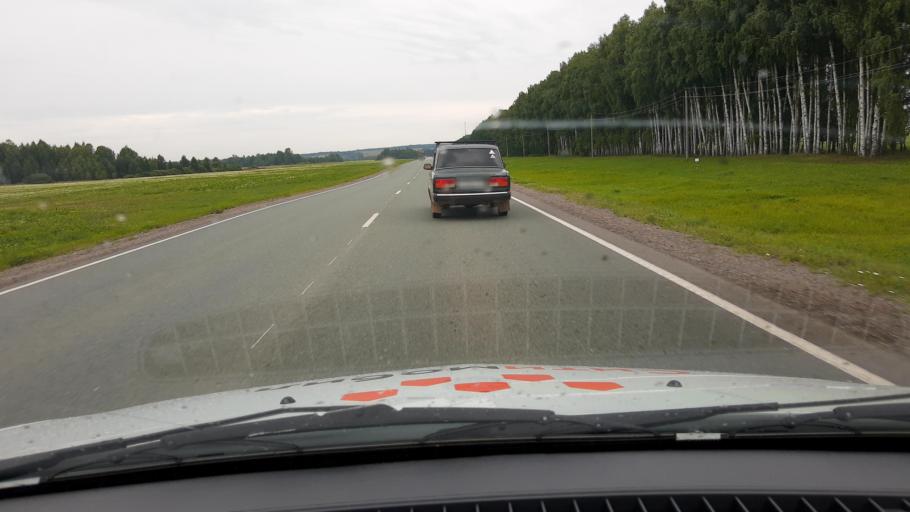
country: RU
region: Bashkortostan
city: Krasnaya Gorka
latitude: 55.1384
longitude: 56.6652
